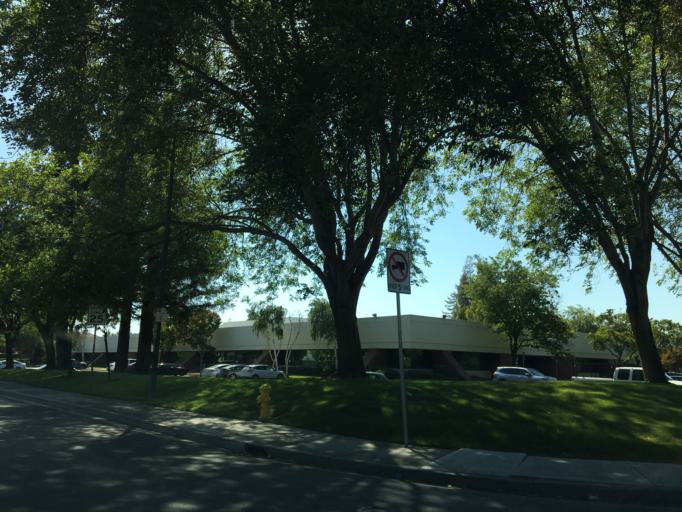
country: US
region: California
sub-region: Santa Clara County
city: Milpitas
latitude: 37.3897
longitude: -121.8951
